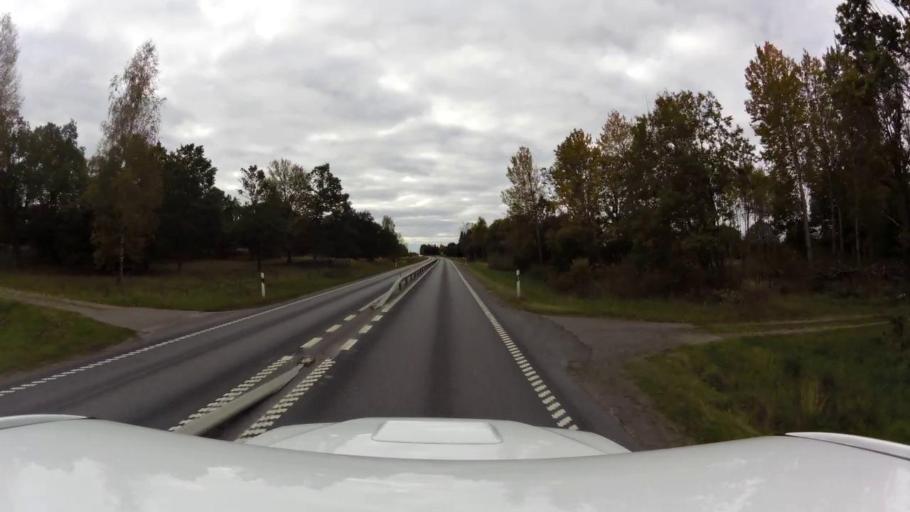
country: SE
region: OEstergoetland
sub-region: Linkopings Kommun
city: Malmslatt
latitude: 58.3649
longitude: 15.5444
